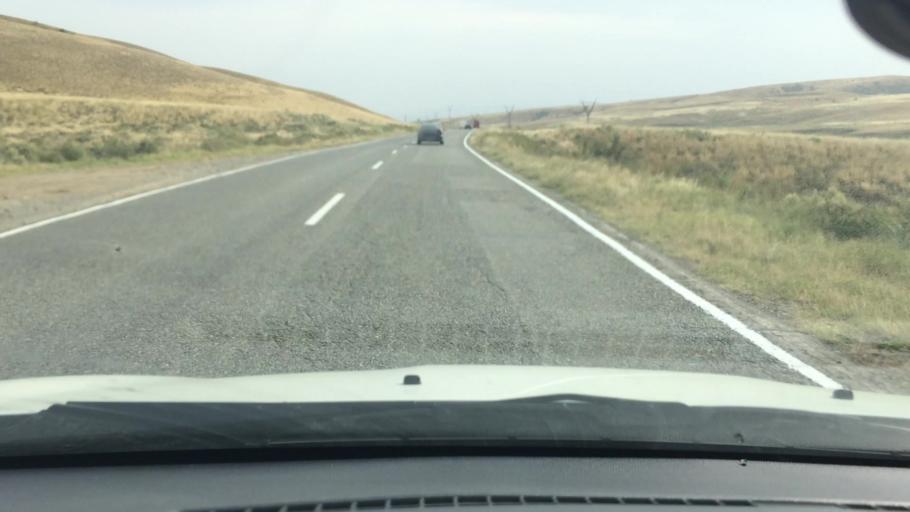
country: GE
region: Kvemo Kartli
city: Rust'avi
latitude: 41.5048
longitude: 44.9537
